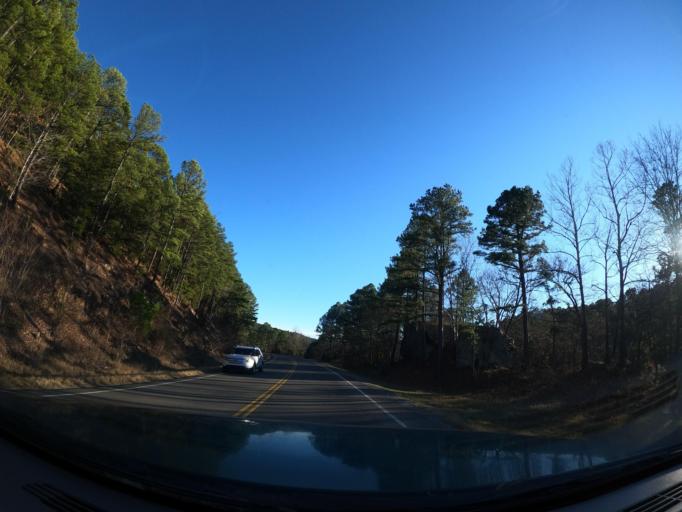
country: US
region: Oklahoma
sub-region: Latimer County
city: Wilburton
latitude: 34.9763
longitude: -95.3591
